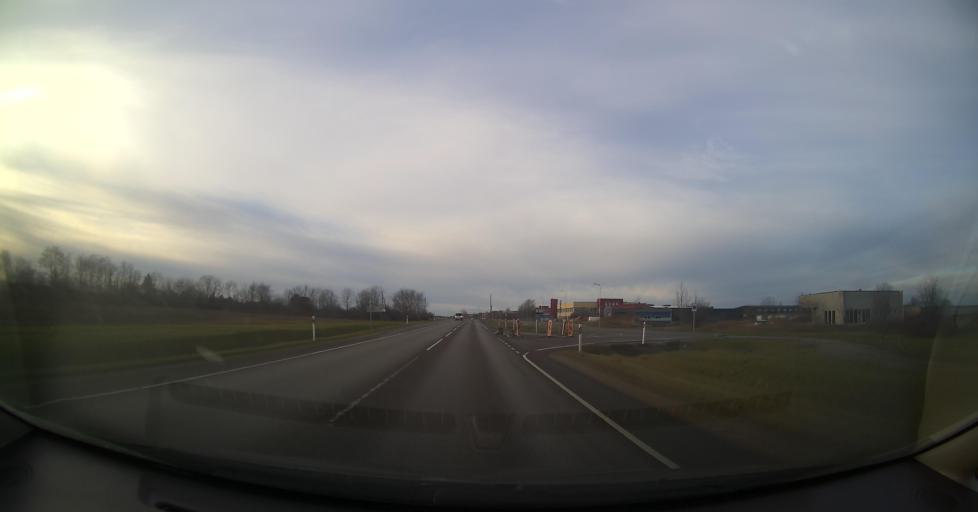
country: EE
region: Ida-Virumaa
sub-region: Sillamaee linn
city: Sillamae
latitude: 59.3874
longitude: 27.8072
